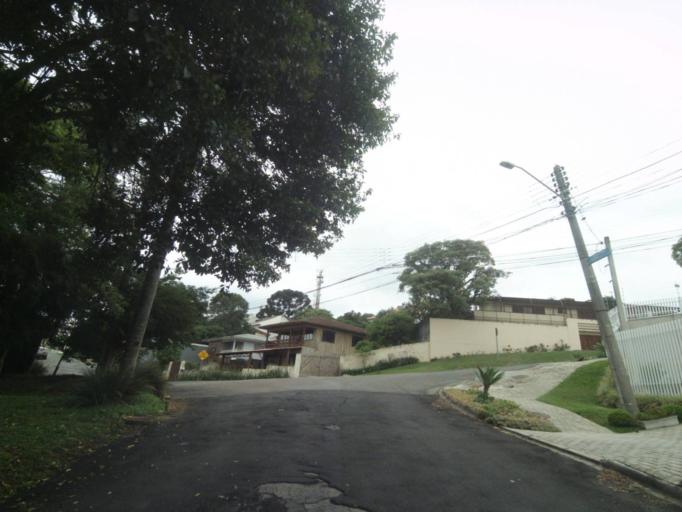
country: BR
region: Parana
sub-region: Curitiba
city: Curitiba
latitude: -25.4017
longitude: -49.2915
